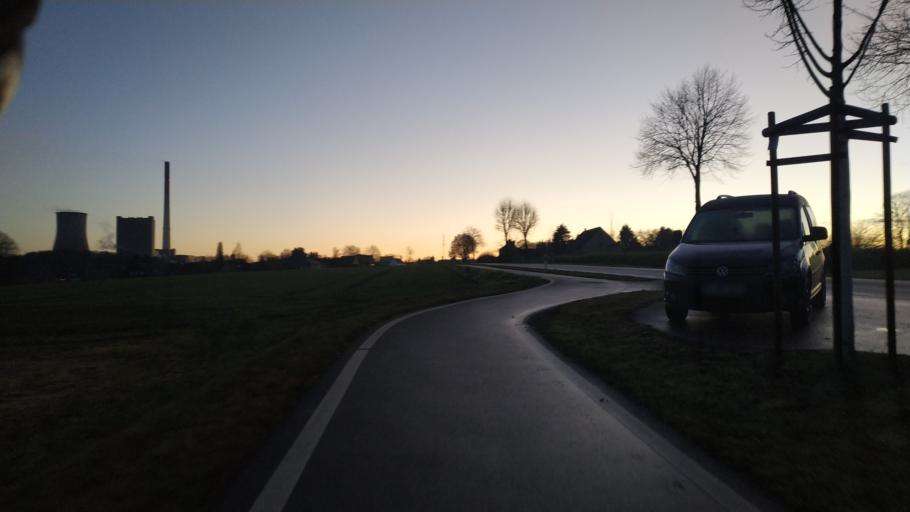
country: DE
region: North Rhine-Westphalia
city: Ibbenburen
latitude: 52.3013
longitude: 7.7464
